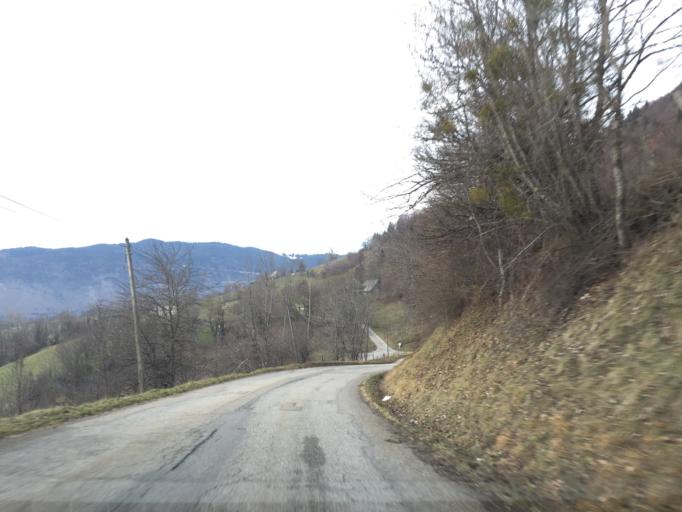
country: FR
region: Rhone-Alpes
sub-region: Departement de la Haute-Savoie
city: Doussard
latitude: 45.7351
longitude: 6.1529
